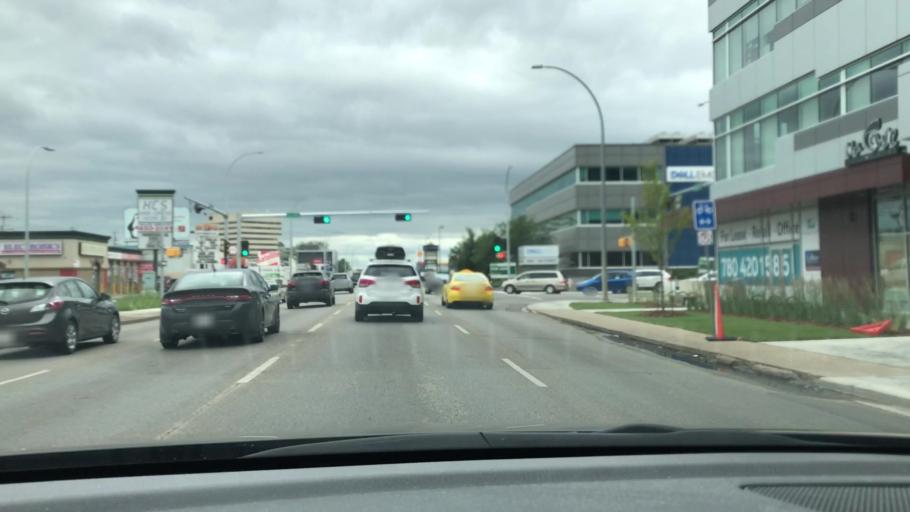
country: CA
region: Alberta
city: Edmonton
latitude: 53.4985
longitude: -113.4977
